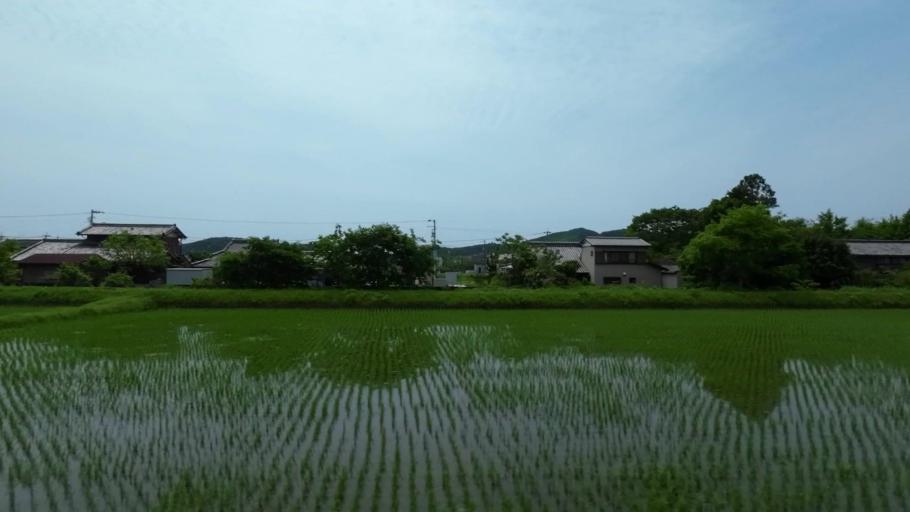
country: JP
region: Kochi
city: Kochi-shi
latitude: 33.5784
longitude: 133.6235
